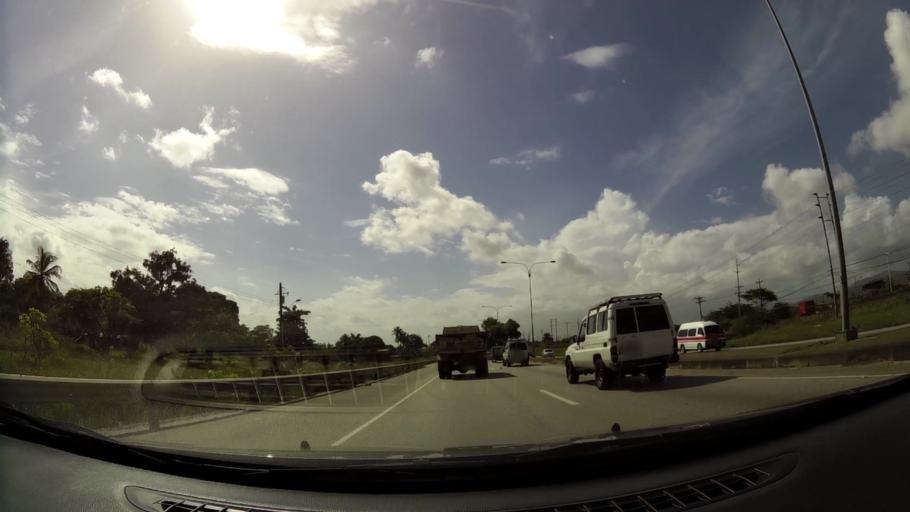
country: TT
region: Borough of Arima
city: Arima
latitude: 10.6070
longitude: -61.2781
